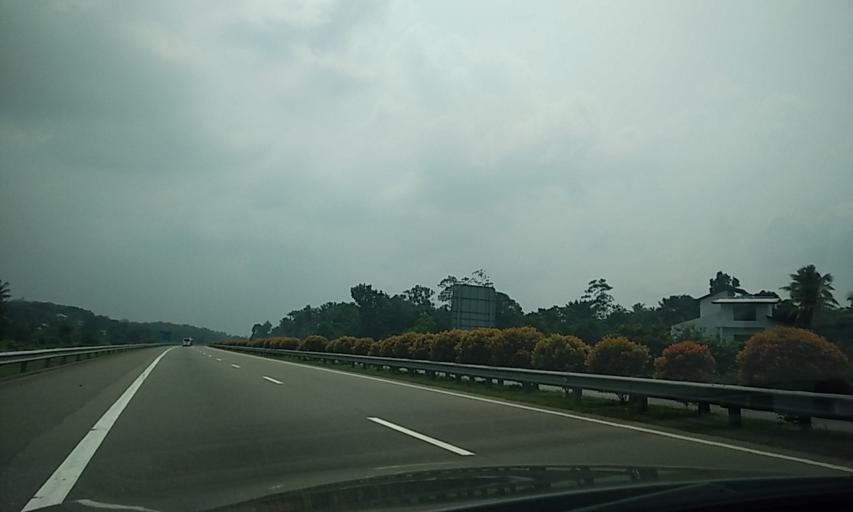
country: LK
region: Western
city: Homagama
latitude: 6.8734
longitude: 79.9782
